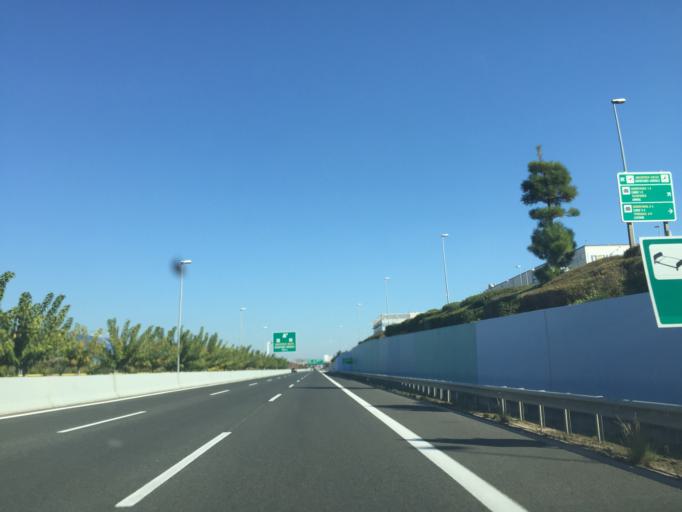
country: GR
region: Attica
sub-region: Nomarchia Anatolikis Attikis
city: Markopoulo
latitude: 37.9224
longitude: 23.9313
